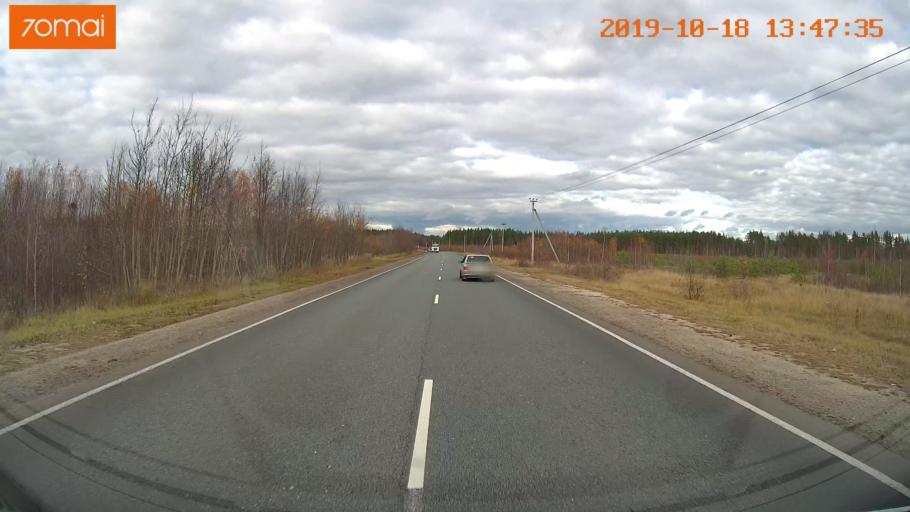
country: RU
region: Moskovskaya
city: Radovitskiy
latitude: 54.9771
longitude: 39.9514
